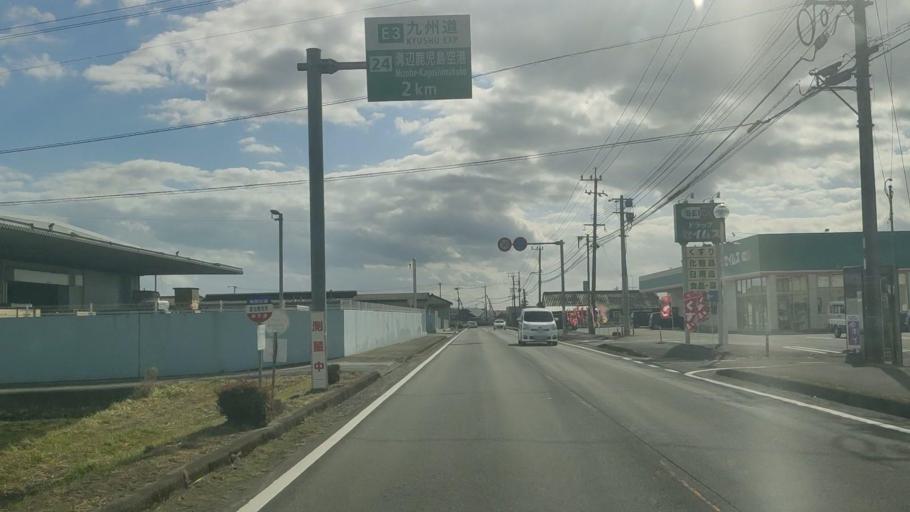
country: JP
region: Kagoshima
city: Kajiki
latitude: 31.8081
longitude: 130.7090
